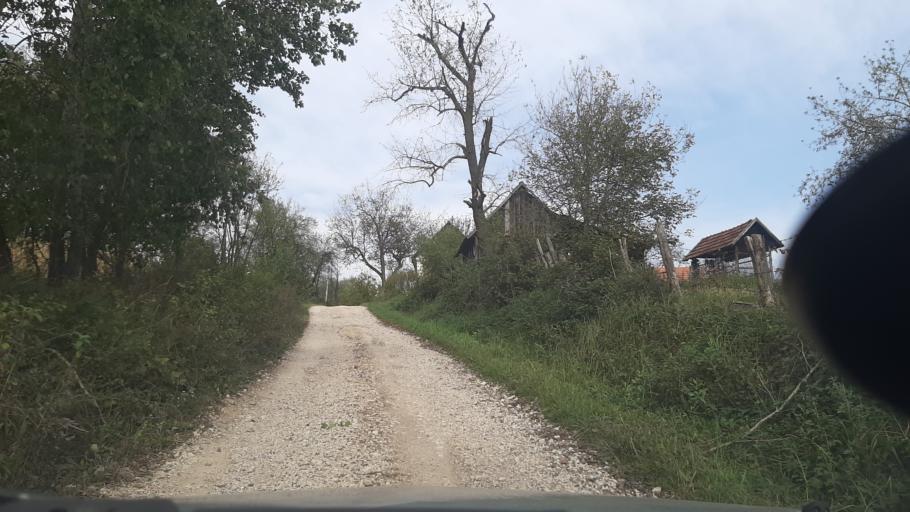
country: BA
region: Republika Srpska
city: Maglajani
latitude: 44.8772
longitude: 17.4730
